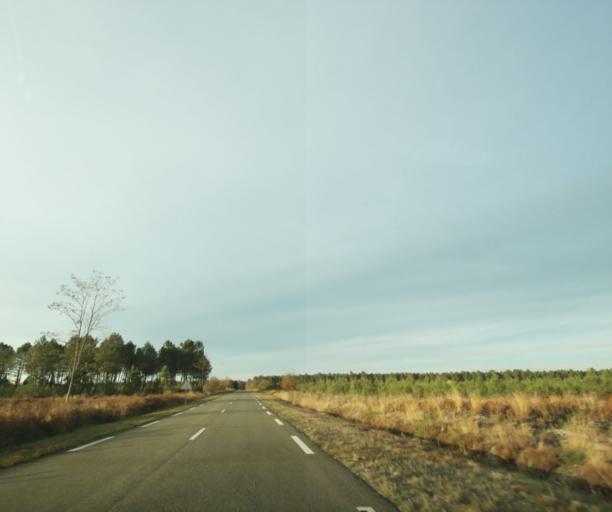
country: FR
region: Aquitaine
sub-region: Departement des Landes
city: Gabarret
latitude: 44.1489
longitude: -0.1265
